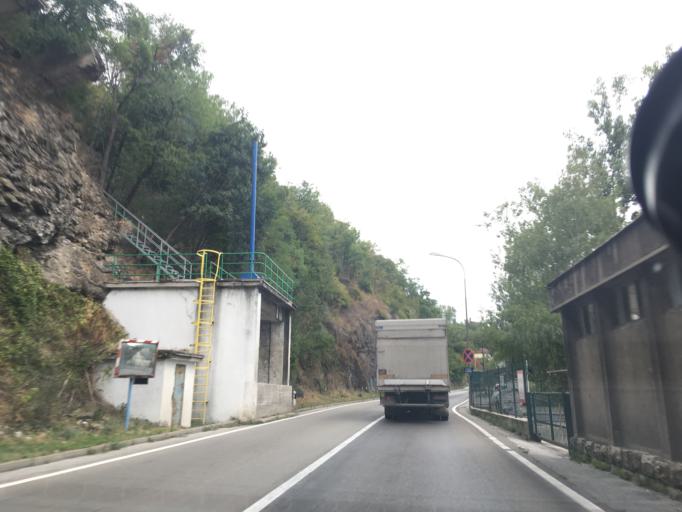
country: RS
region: Central Serbia
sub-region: Moravicki Okrug
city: Lucani
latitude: 43.9089
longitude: 20.2316
